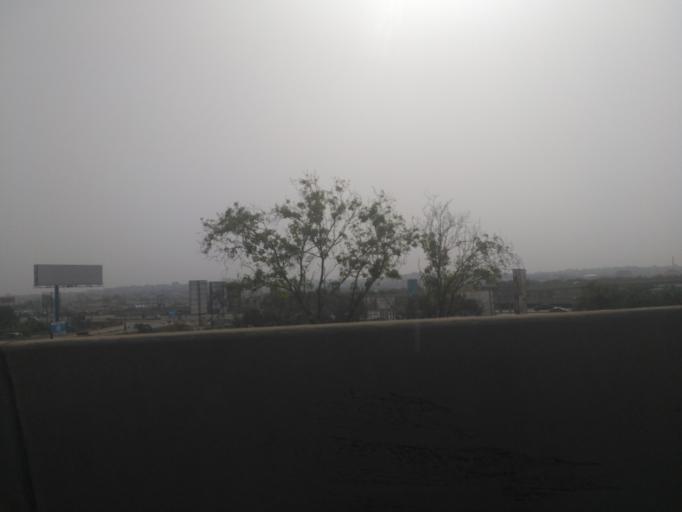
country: GH
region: Greater Accra
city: Gbawe
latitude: 5.5721
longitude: -0.2840
